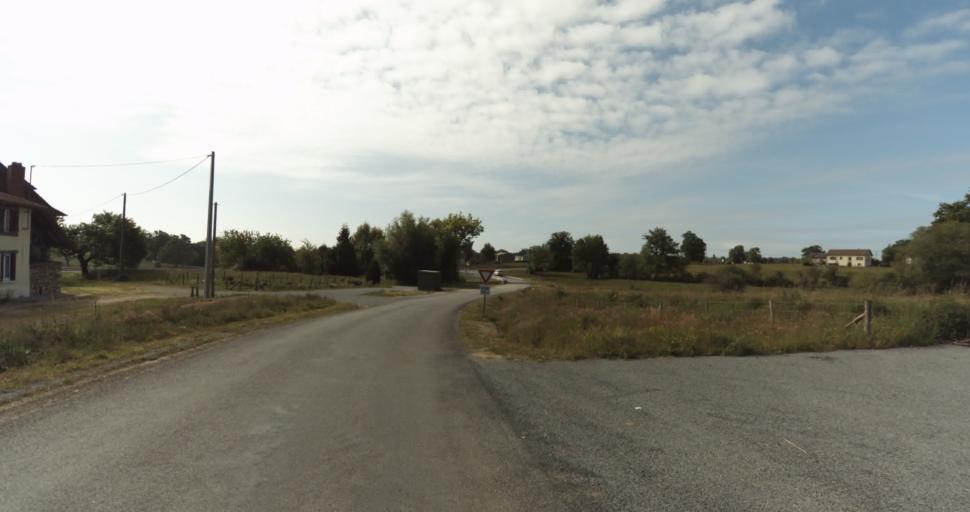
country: FR
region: Limousin
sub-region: Departement de la Haute-Vienne
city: Bosmie-l'Aiguille
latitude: 45.7079
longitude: 1.2406
